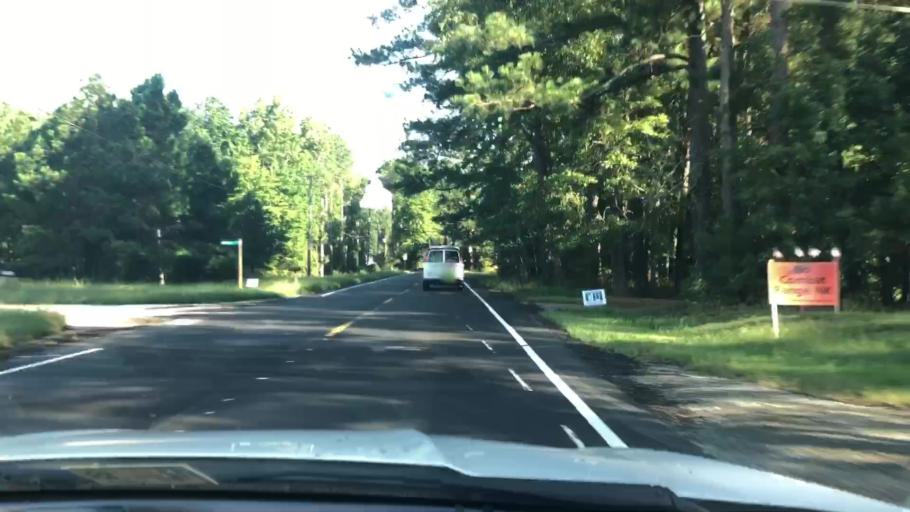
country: US
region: Virginia
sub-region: King William County
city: West Point
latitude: 37.4670
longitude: -76.8436
